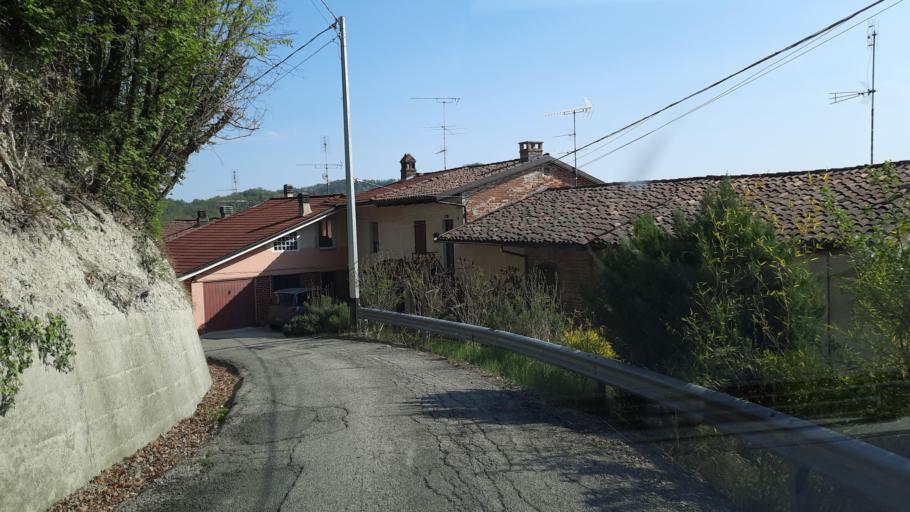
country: IT
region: Piedmont
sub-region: Provincia di Alessandria
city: Villamiroglio
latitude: 45.1339
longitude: 8.1708
